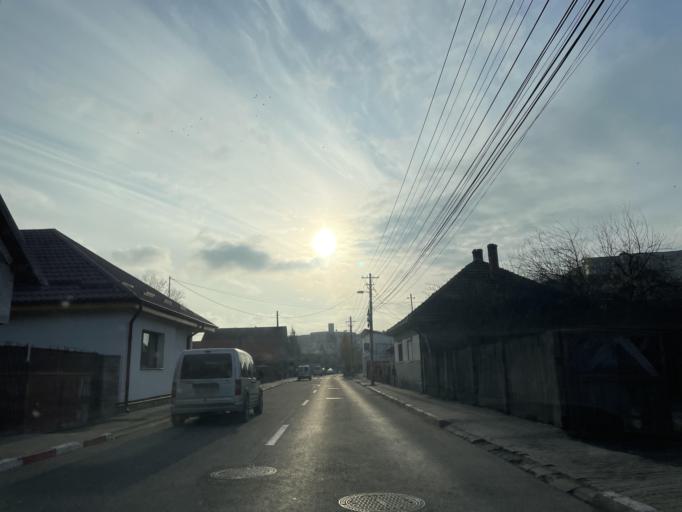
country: RO
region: Mures
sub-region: Municipiul Reghin
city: Reghin
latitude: 46.7757
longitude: 24.7060
